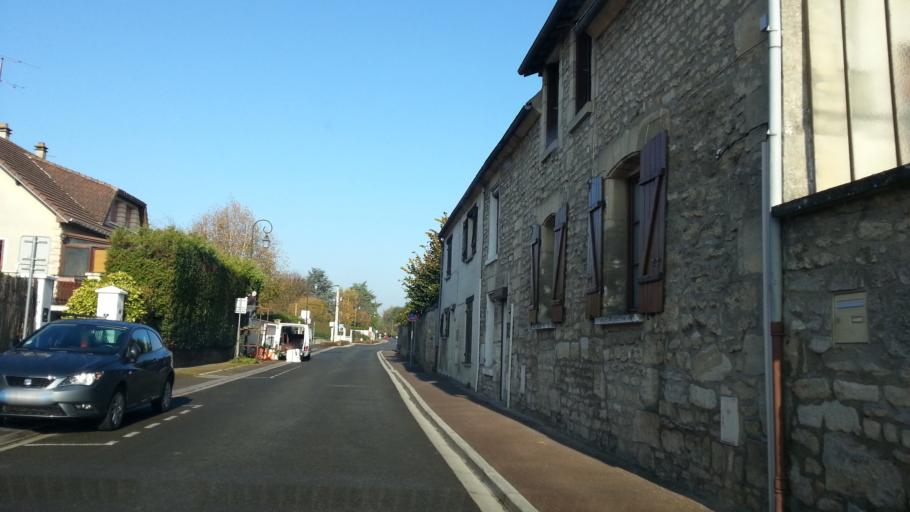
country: FR
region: Picardie
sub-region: Departement de l'Oise
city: Balagny-sur-Therain
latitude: 49.3001
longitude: 2.3327
